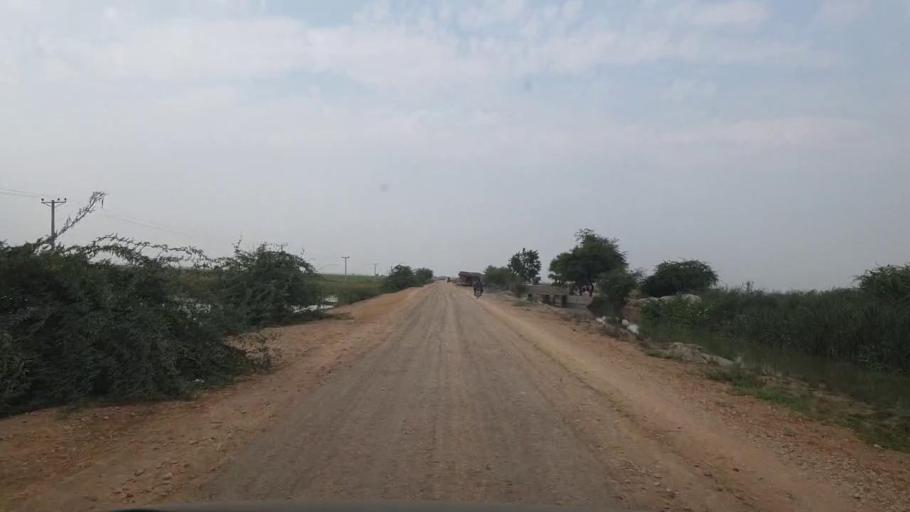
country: PK
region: Sindh
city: Kario
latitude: 24.6095
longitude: 68.5936
